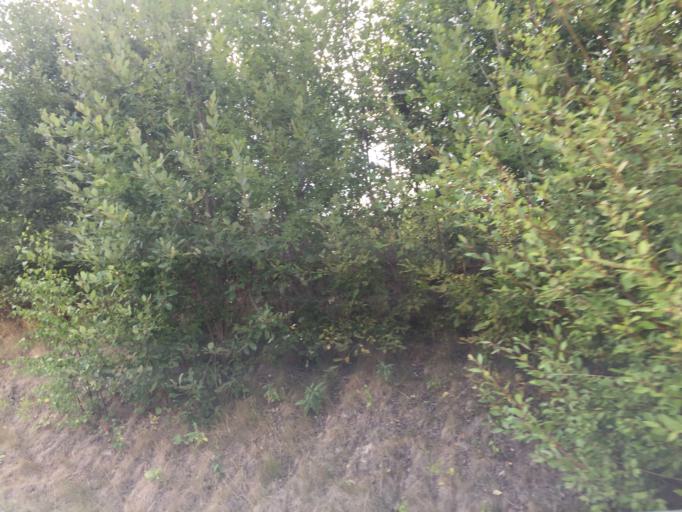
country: NO
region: Ostfold
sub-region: Askim
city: Askim
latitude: 59.5897
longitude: 11.1343
